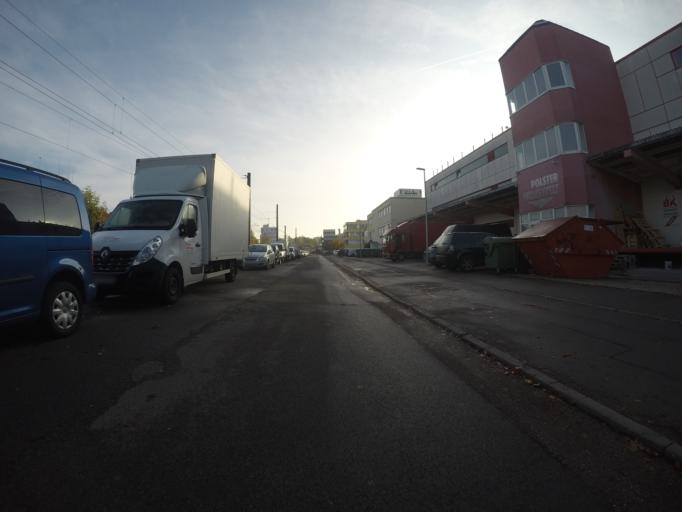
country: DE
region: Baden-Wuerttemberg
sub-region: Regierungsbezirk Stuttgart
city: Leinfelden-Echterdingen
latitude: 48.7102
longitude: 9.1995
